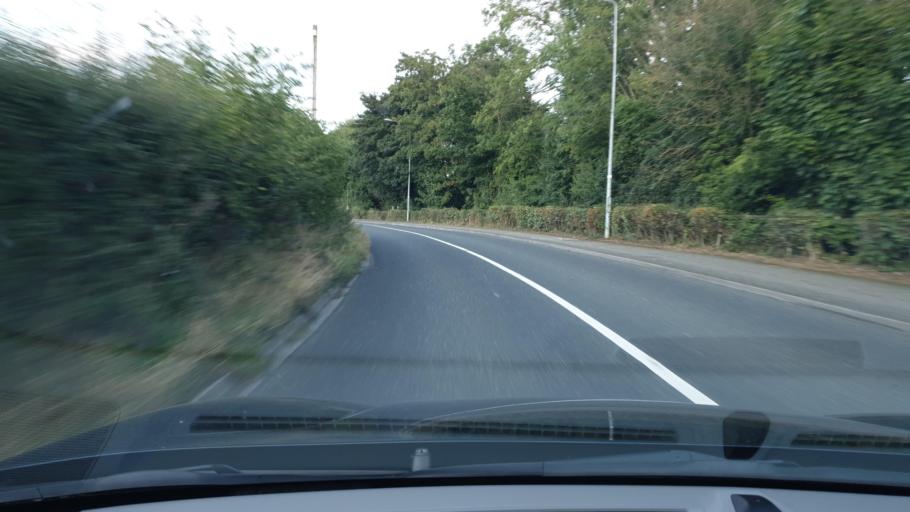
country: IE
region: Leinster
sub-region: Kildare
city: Kill
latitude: 53.2542
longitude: -6.5633
